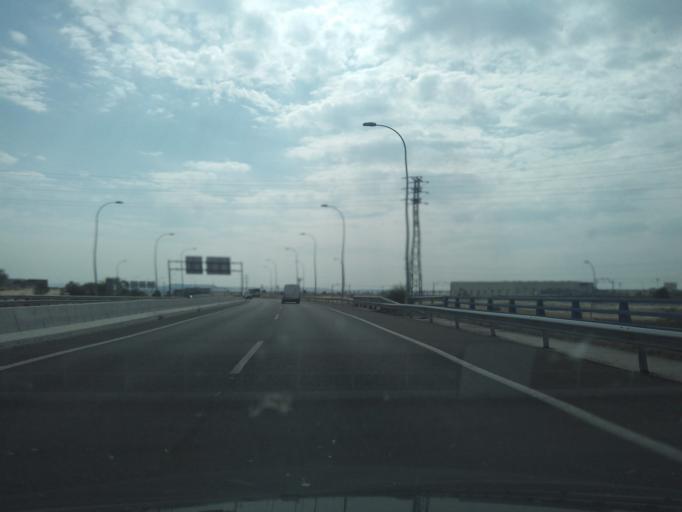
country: ES
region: Madrid
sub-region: Provincia de Madrid
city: Coslada
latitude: 40.4397
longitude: -3.5605
